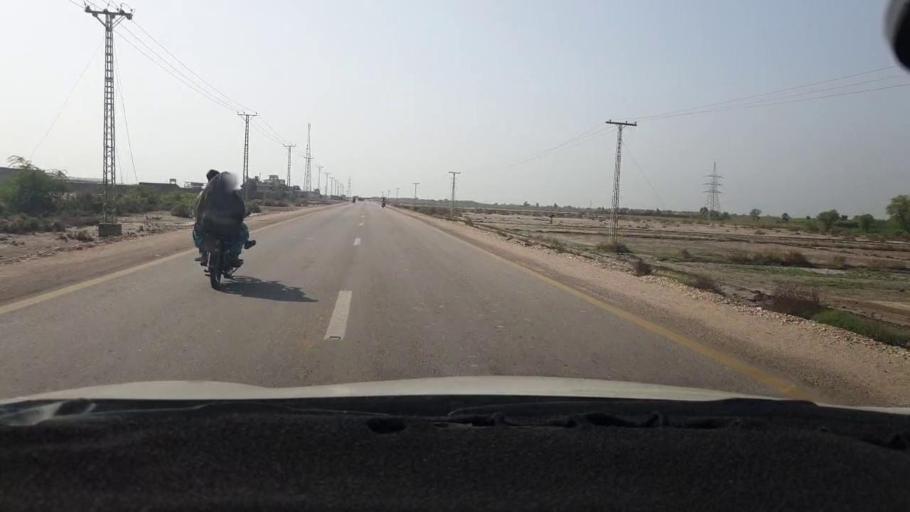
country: PK
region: Sindh
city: Jhol
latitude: 25.9586
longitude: 68.9751
